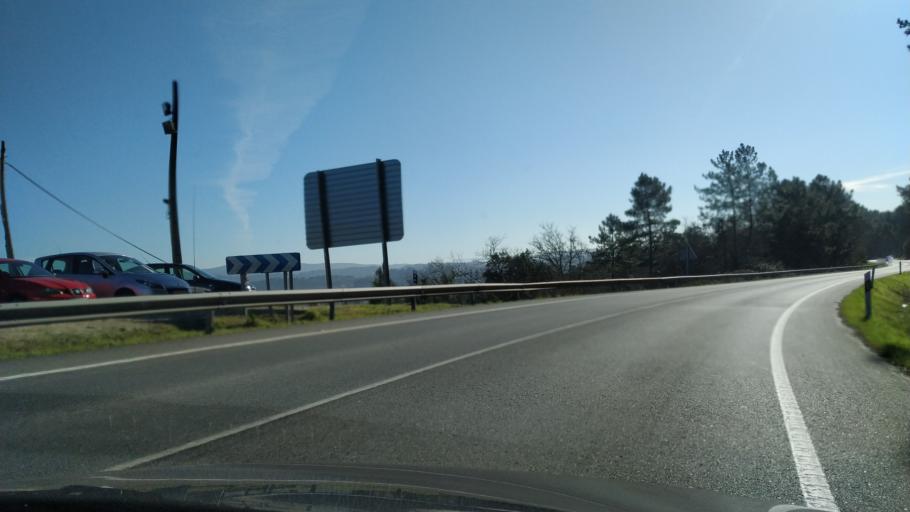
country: ES
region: Galicia
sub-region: Provincia da Coruna
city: Ribeira
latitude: 42.7479
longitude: -8.3416
